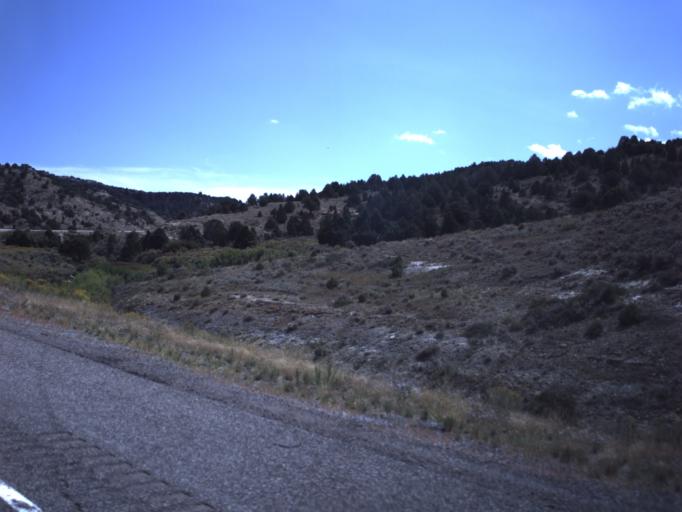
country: US
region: Utah
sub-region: Sevier County
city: Salina
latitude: 38.8022
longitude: -111.5196
